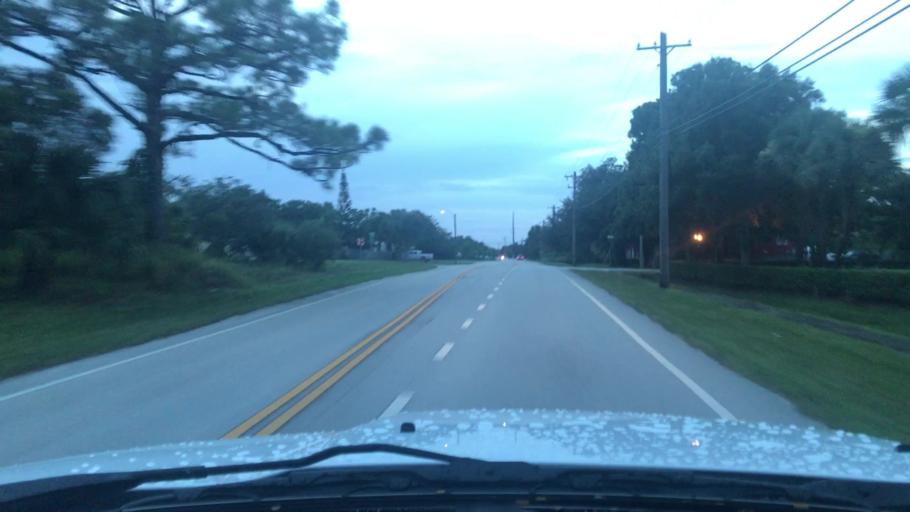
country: US
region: Florida
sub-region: Indian River County
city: Florida Ridge
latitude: 27.5990
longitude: -80.3849
